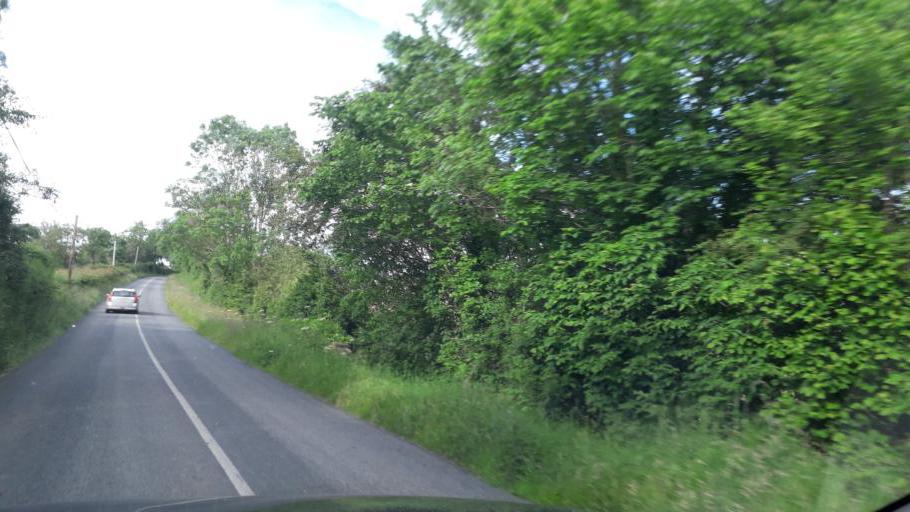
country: IE
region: Leinster
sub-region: Loch Garman
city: Courtown
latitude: 52.5488
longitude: -6.2514
